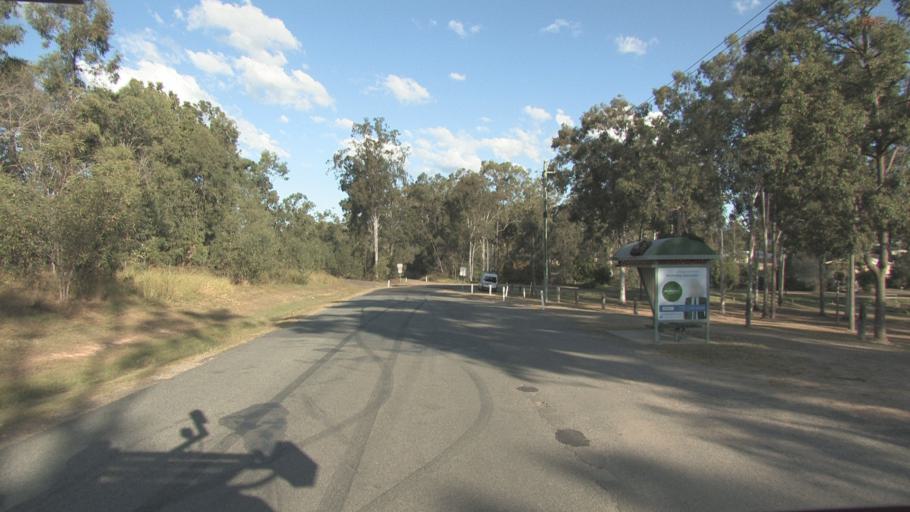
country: AU
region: Queensland
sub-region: Logan
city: North Maclean
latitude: -27.7475
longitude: 152.9407
